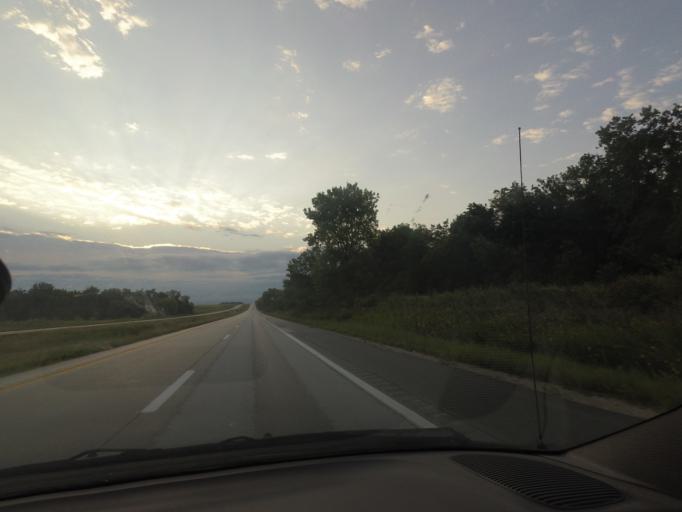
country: US
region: Missouri
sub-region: Shelby County
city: Shelbina
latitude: 39.7241
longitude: -92.1700
